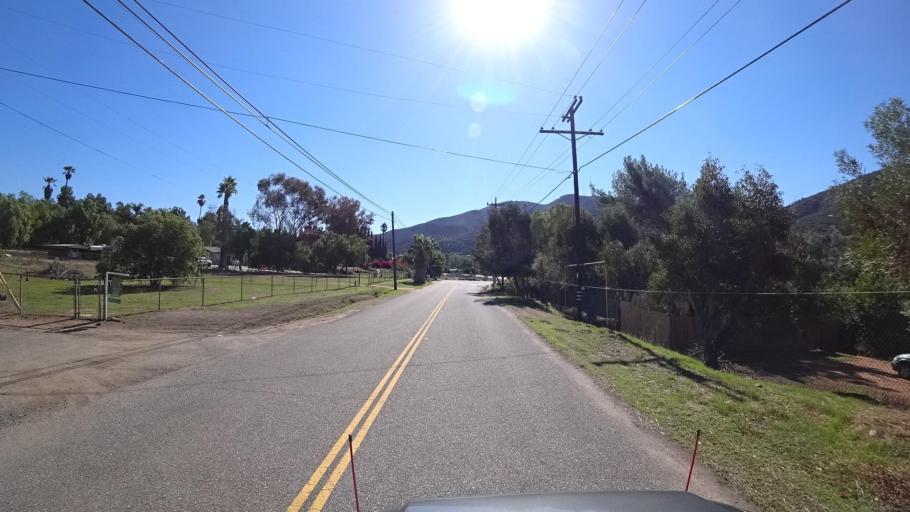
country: US
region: California
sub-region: San Diego County
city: Rancho San Diego
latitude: 32.7264
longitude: -116.9180
